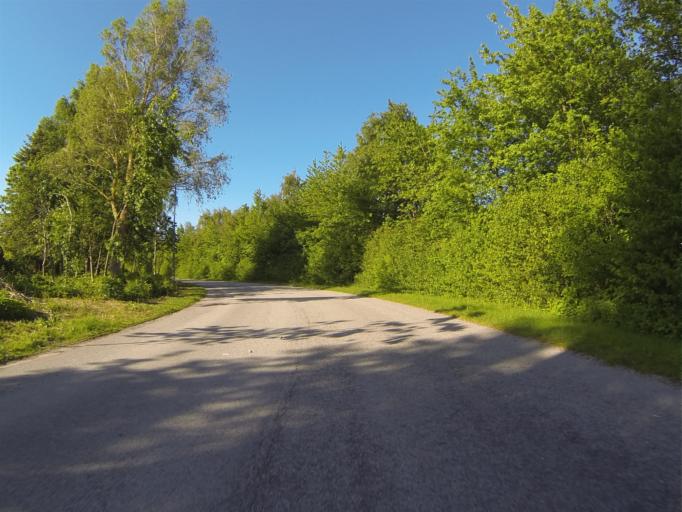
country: SE
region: Skane
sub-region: Lunds Kommun
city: Genarp
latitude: 55.7167
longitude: 13.3639
